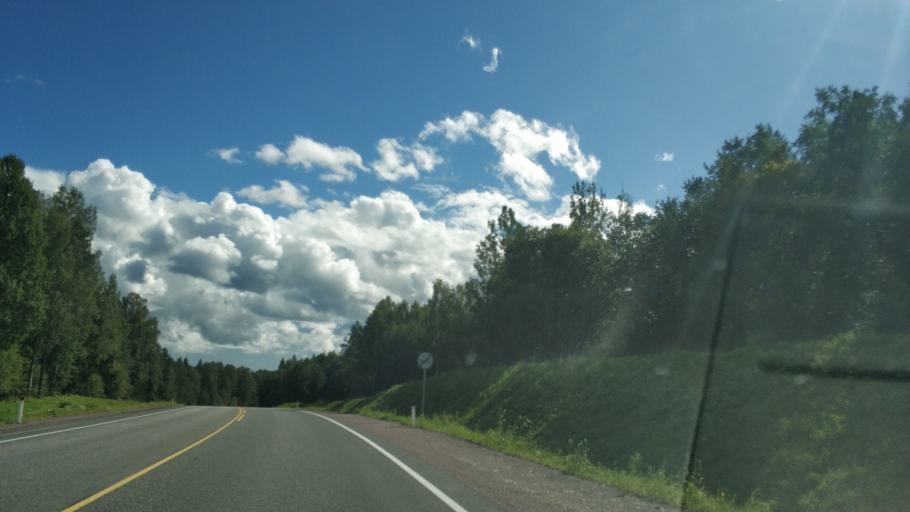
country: RU
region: Republic of Karelia
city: Ruskeala
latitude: 61.8956
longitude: 30.6379
